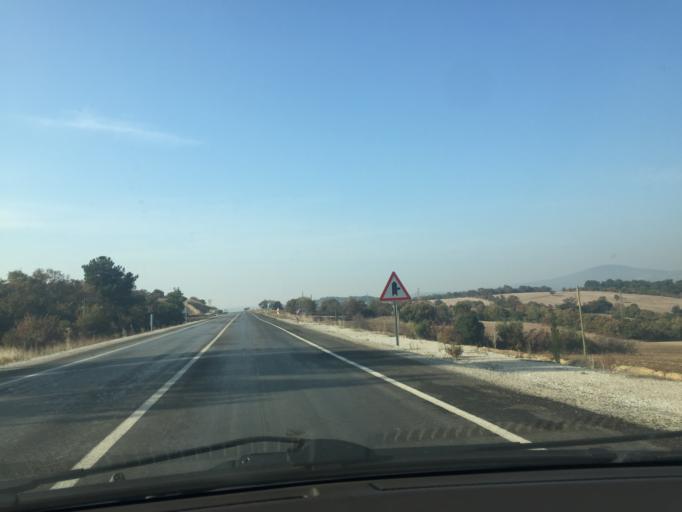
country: TR
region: Canakkale
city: Yigitler
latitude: 39.8867
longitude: 26.6904
